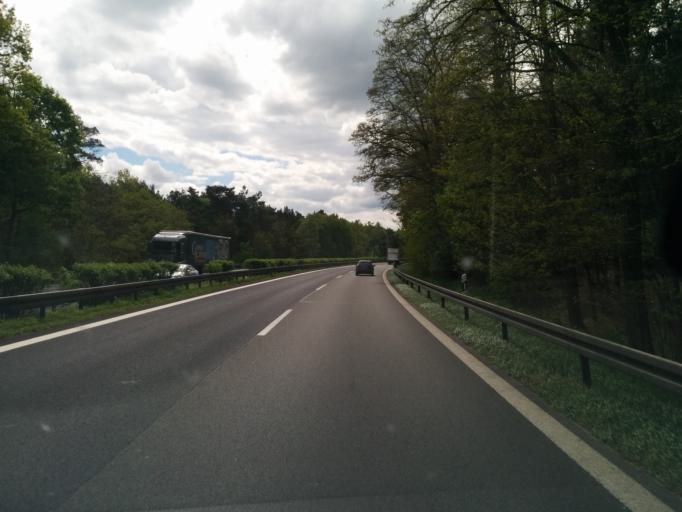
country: DE
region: Brandenburg
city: Werder
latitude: 52.4256
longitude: 12.9293
